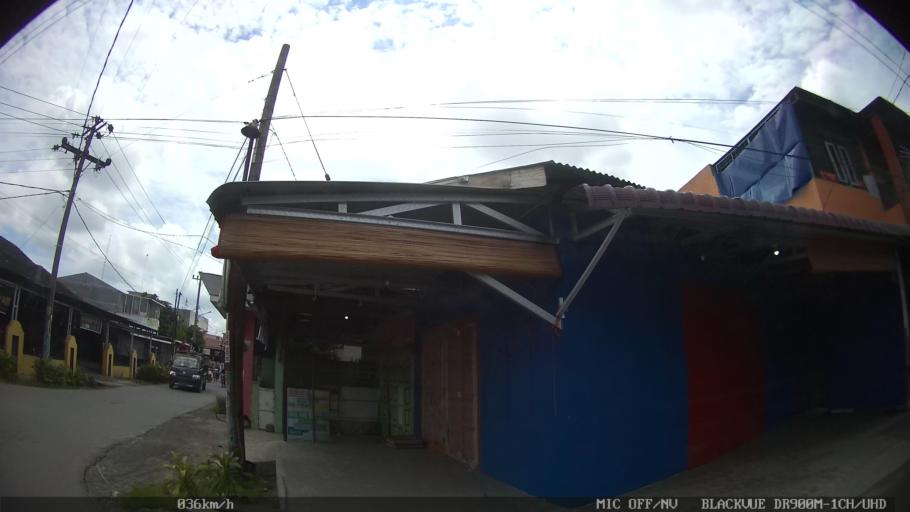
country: ID
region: North Sumatra
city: Medan
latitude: 3.6071
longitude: 98.7497
